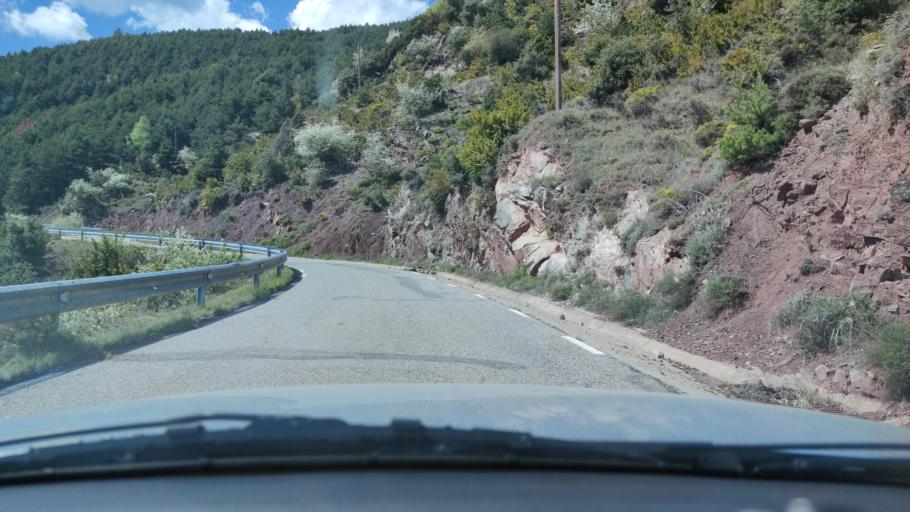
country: ES
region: Catalonia
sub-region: Provincia de Lleida
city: Coll de Nargo
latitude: 42.3080
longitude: 1.2823
